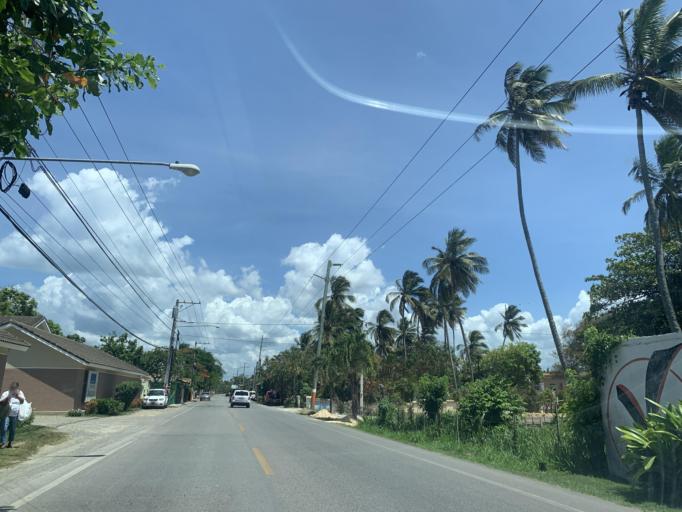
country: DO
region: Puerto Plata
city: Cabarete
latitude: 19.7401
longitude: -70.3920
